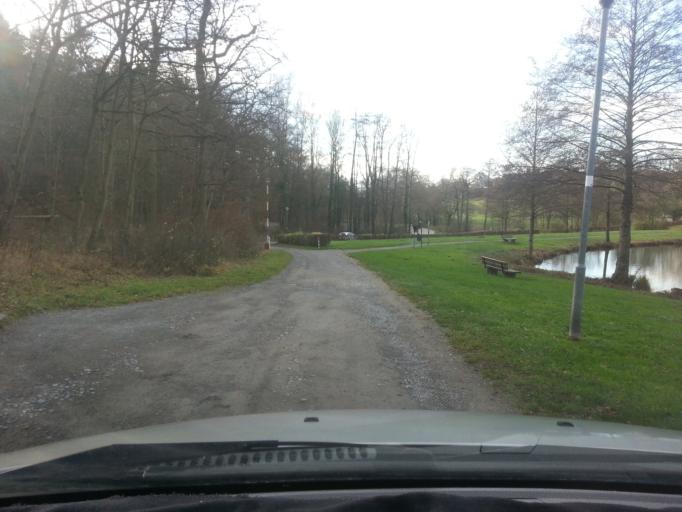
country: DE
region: Baden-Wuerttemberg
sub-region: Karlsruhe Region
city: Zaisenhausen
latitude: 49.1797
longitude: 8.8124
